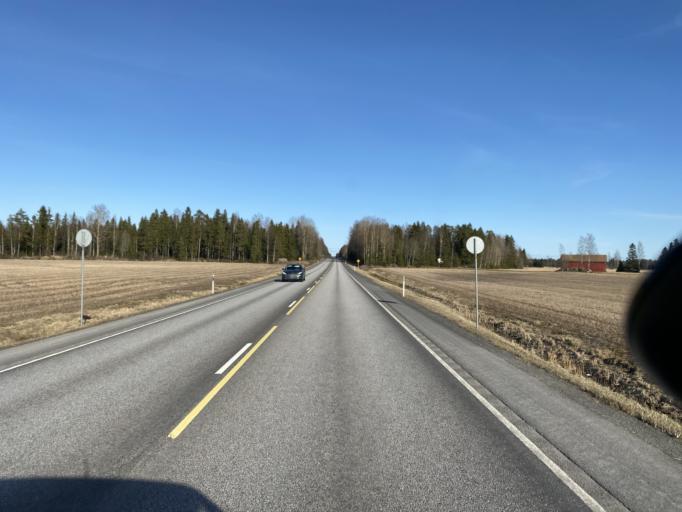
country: FI
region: Satakunta
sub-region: Rauma
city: Eura
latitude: 61.1312
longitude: 22.0456
